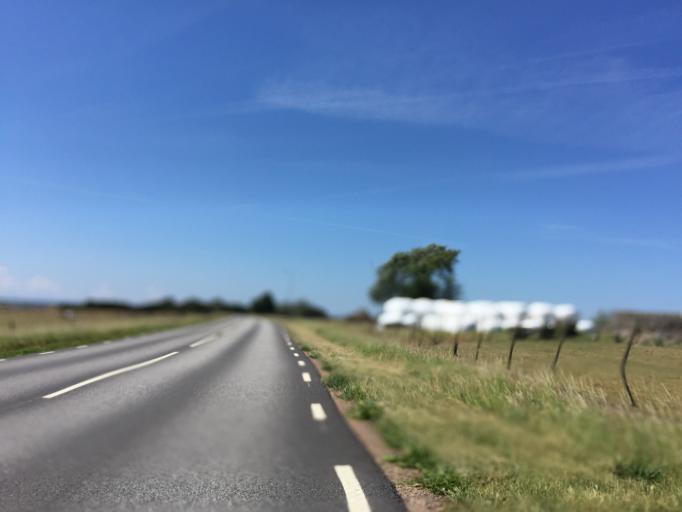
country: SE
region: Skane
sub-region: Vellinge Kommun
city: Hollviken
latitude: 55.3940
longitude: 12.9995
